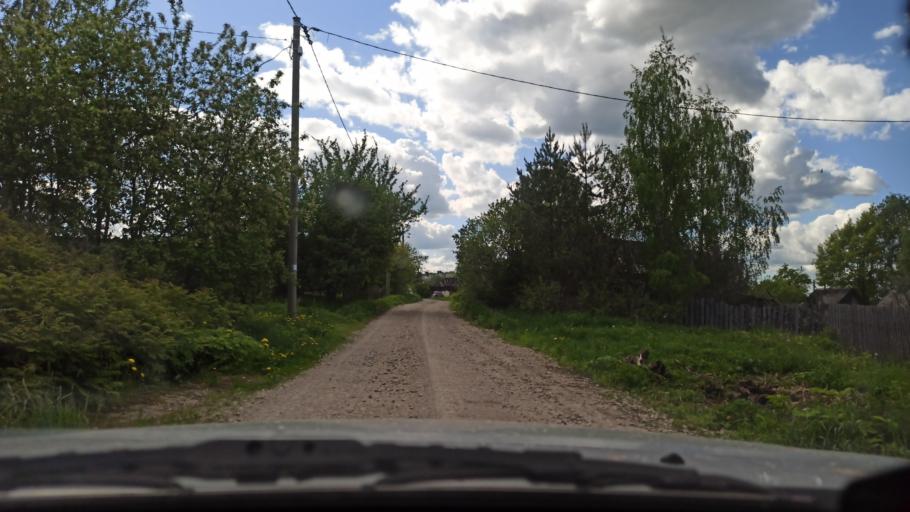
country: RU
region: Vologda
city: Vologda
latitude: 59.3431
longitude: 39.8225
